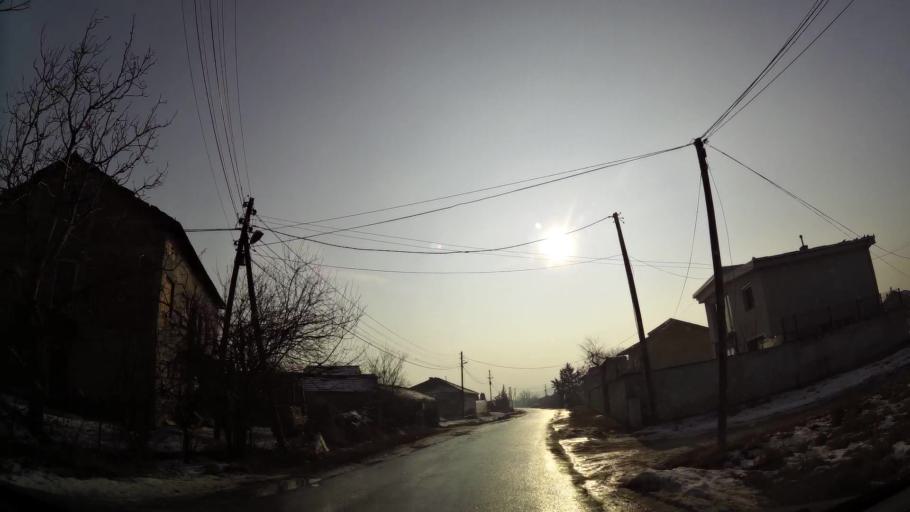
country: MK
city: Kadino
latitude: 41.9561
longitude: 21.6018
